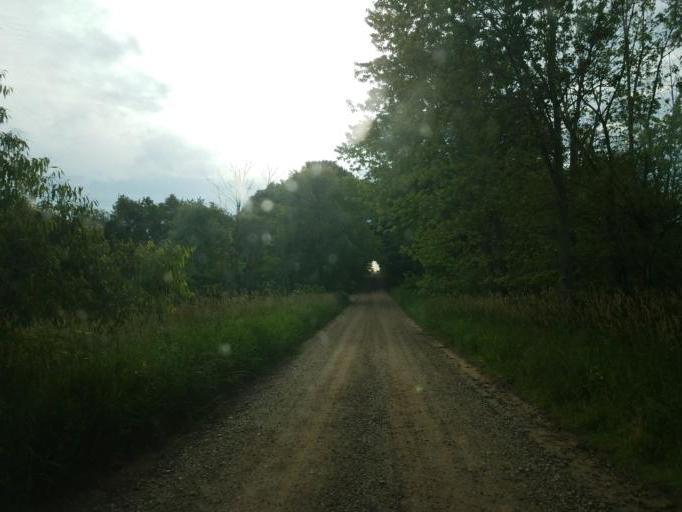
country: US
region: Michigan
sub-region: Barry County
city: Nashville
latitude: 42.6117
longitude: -84.9606
